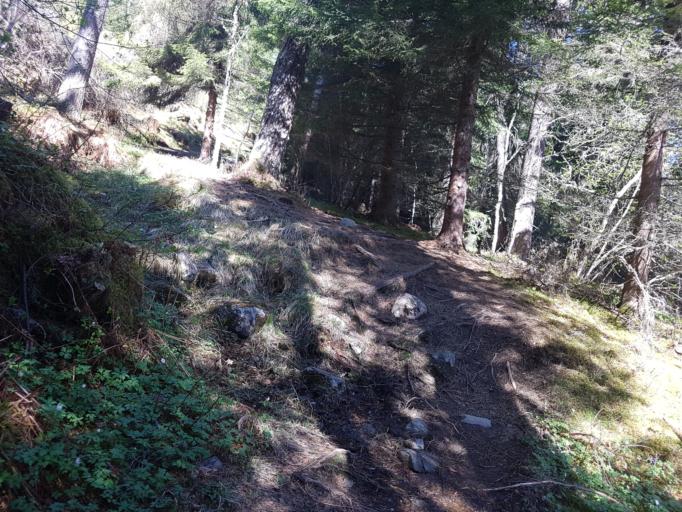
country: NO
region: Sor-Trondelag
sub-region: Trondheim
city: Trondheim
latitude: 63.4325
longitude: 10.3402
